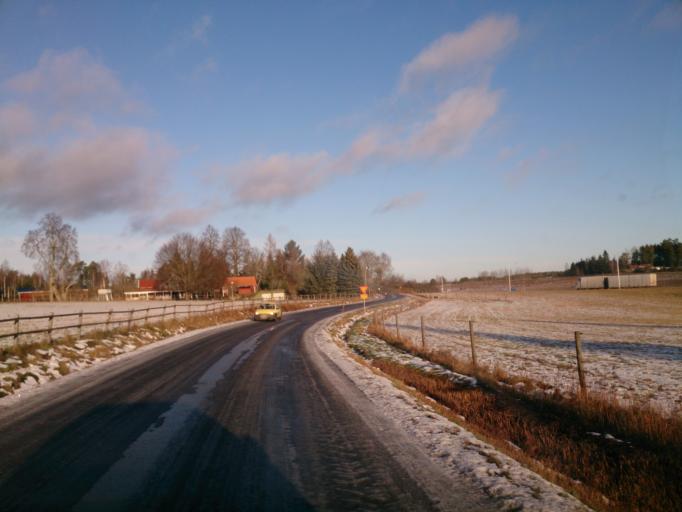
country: SE
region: OEstergoetland
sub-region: Linkopings Kommun
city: Sturefors
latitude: 58.3128
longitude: 15.8715
